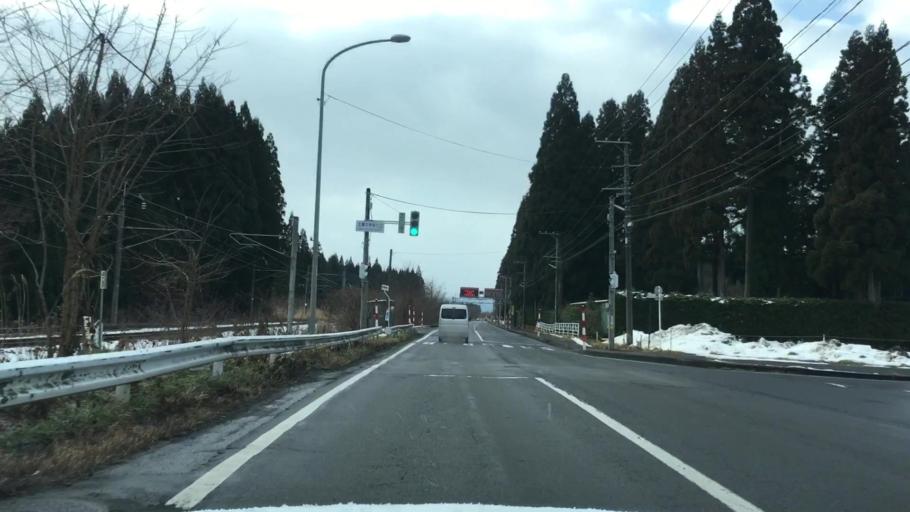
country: JP
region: Akita
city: Odate
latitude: 40.3228
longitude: 140.5813
